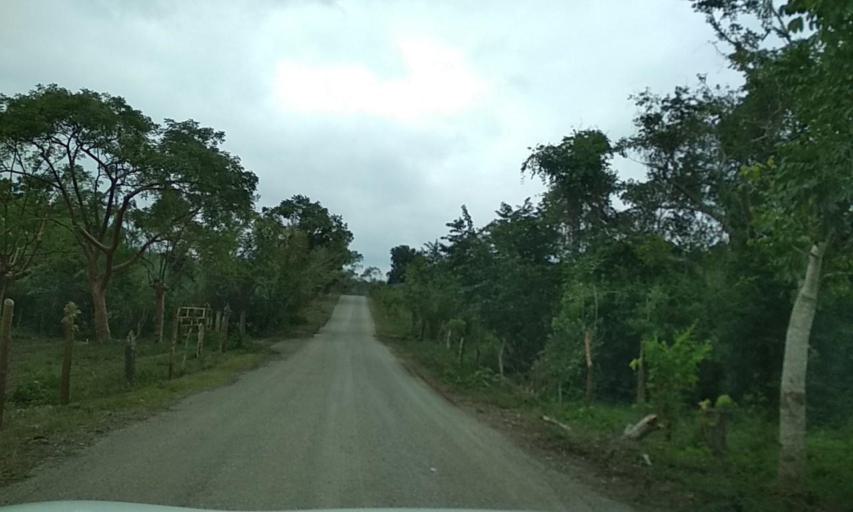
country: MX
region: Veracruz
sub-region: Coatzintla
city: Manuel Maria Contreras
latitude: 20.3448
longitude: -97.4702
